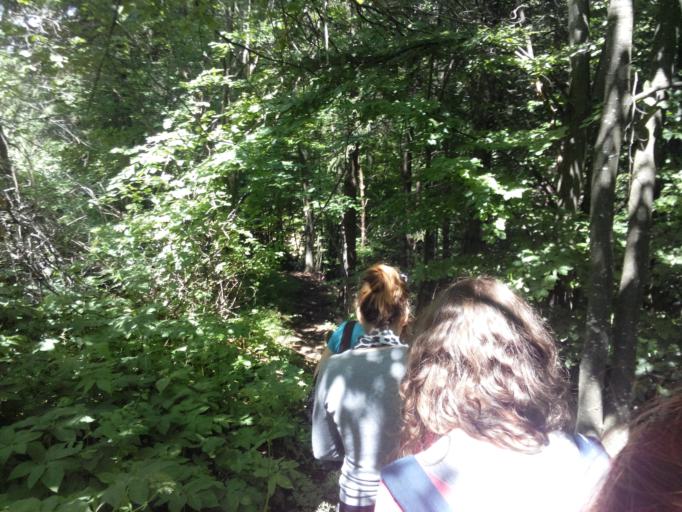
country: RO
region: Brasov
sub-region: Comuna Fundata
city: Fundata
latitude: 45.4520
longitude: 25.3246
